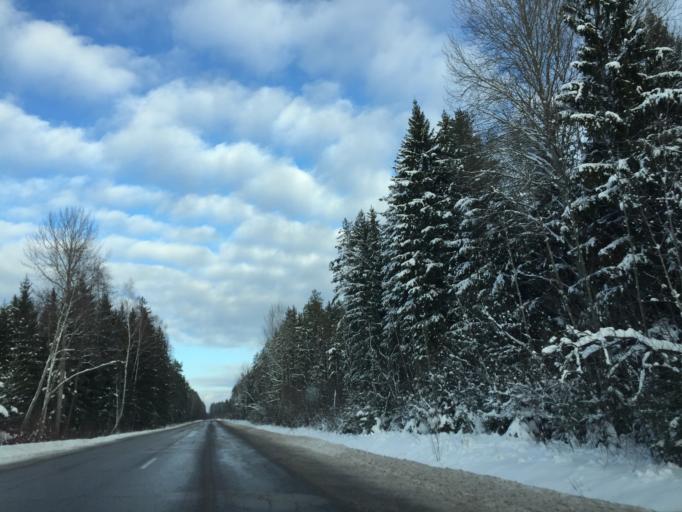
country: LV
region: Ropazu
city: Ropazi
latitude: 56.9899
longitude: 24.6394
